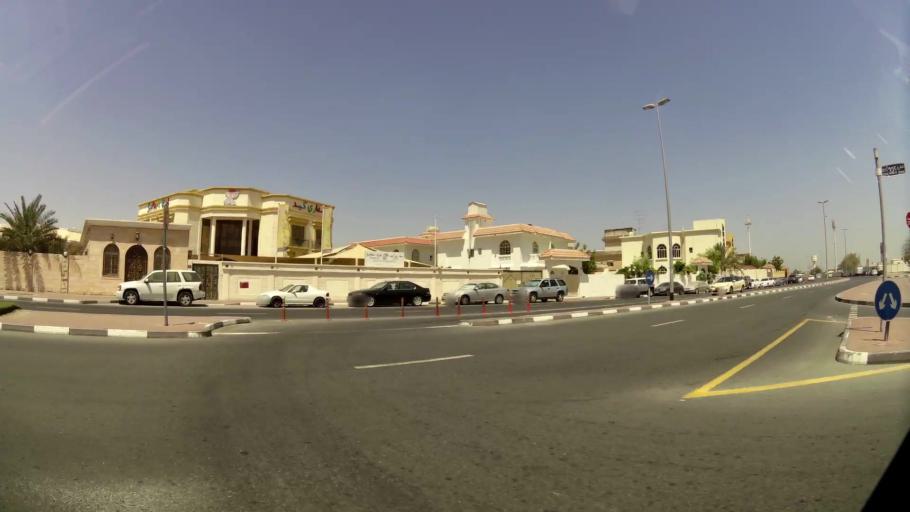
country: AE
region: Dubai
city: Dubai
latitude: 25.2162
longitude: 55.2739
